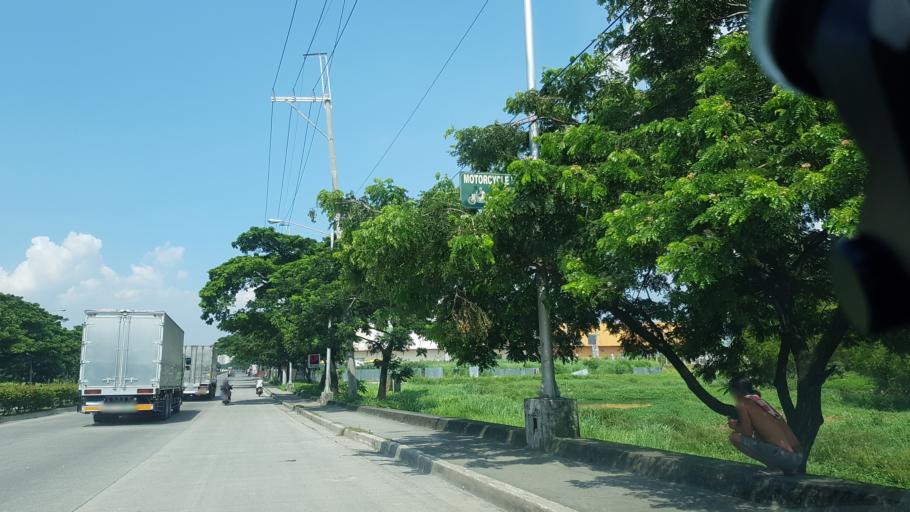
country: PH
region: Calabarzon
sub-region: Province of Rizal
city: Las Pinas
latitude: 14.4756
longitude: 120.9824
